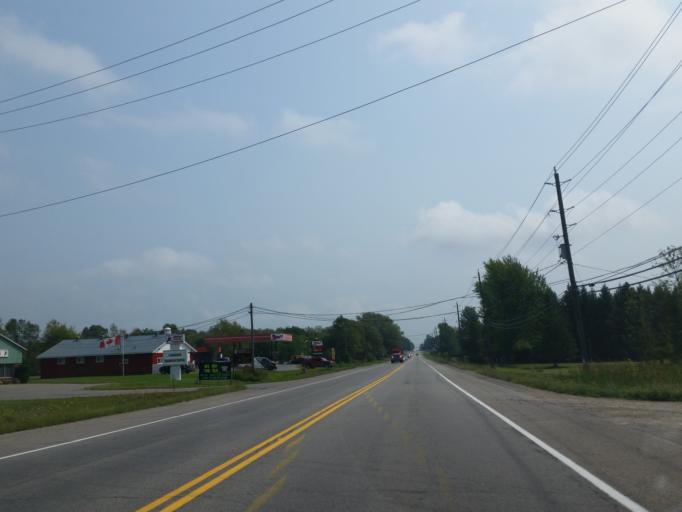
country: CA
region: Ontario
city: Brockville
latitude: 44.6155
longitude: -75.7486
